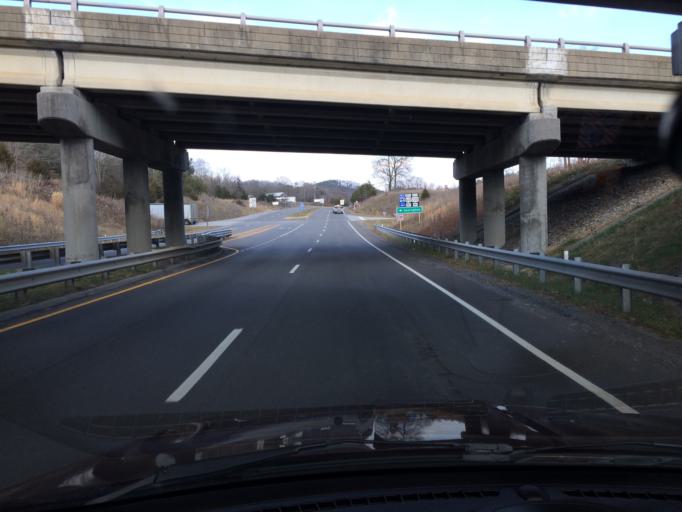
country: US
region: Virginia
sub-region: Alleghany County
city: Clifton Forge
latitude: 37.8269
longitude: -79.7930
